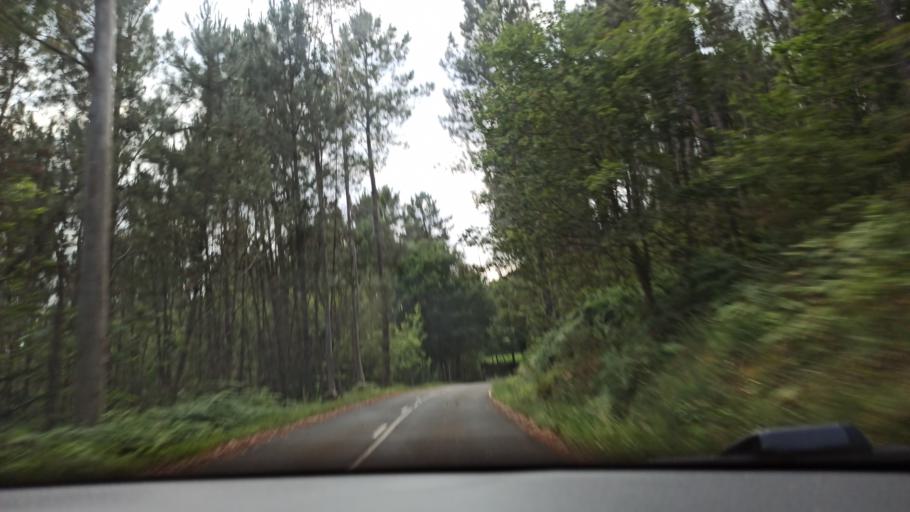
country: ES
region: Galicia
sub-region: Provincia da Coruna
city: Santiso
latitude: 42.8237
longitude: -8.1254
